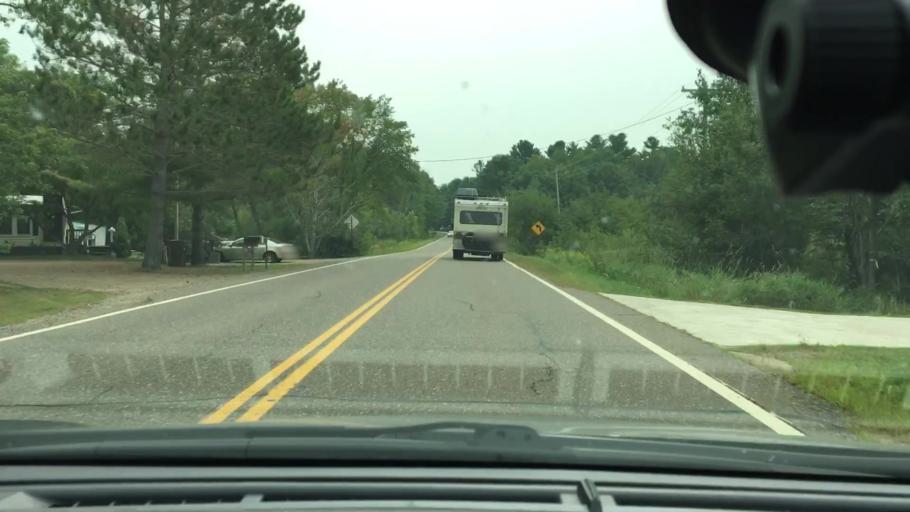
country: US
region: Minnesota
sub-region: Aitkin County
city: Aitkin
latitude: 46.4031
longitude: -93.7762
